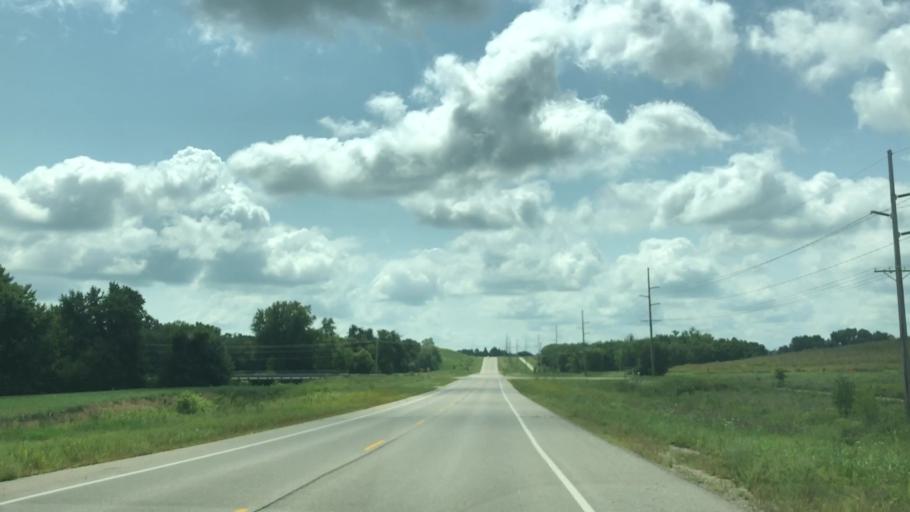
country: US
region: Iowa
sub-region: Marshall County
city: Marshalltown
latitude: 42.0198
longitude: -92.9601
